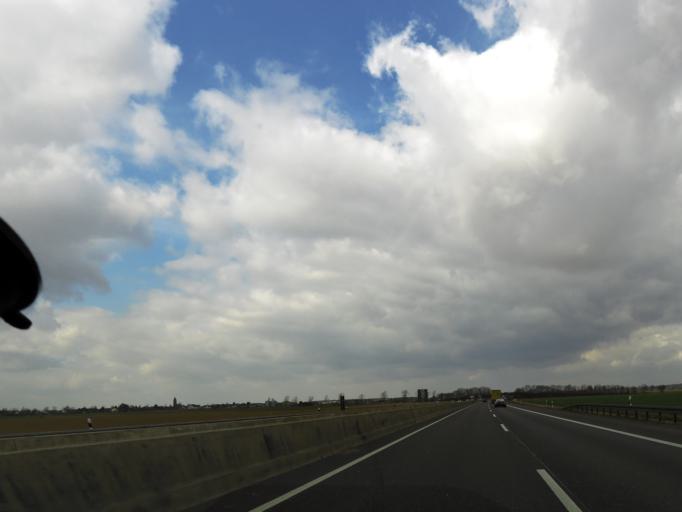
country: DE
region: North Rhine-Westphalia
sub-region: Regierungsbezirk Koln
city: Rheinbach
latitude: 50.6807
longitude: 6.9138
